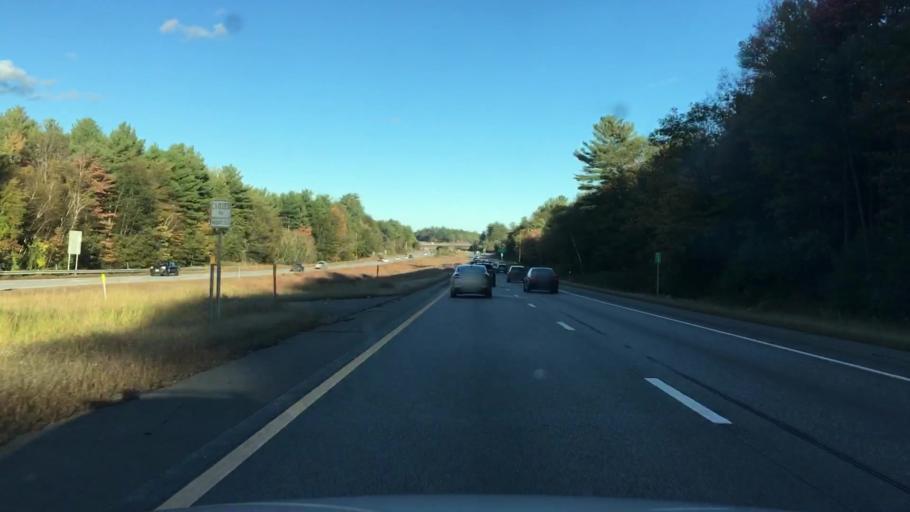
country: US
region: New Hampshire
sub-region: Rockingham County
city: Raymond
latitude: 43.0229
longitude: -71.2090
